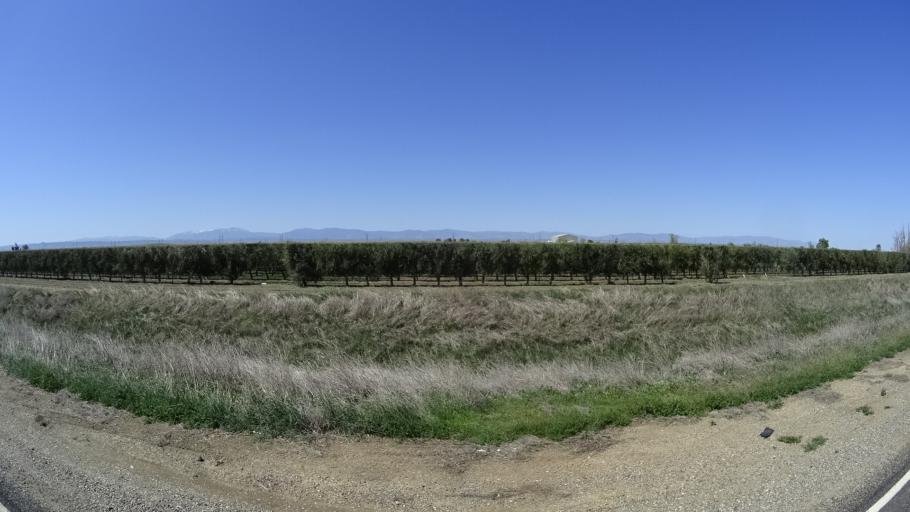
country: US
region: California
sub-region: Glenn County
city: Willows
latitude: 39.6041
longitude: -122.2498
